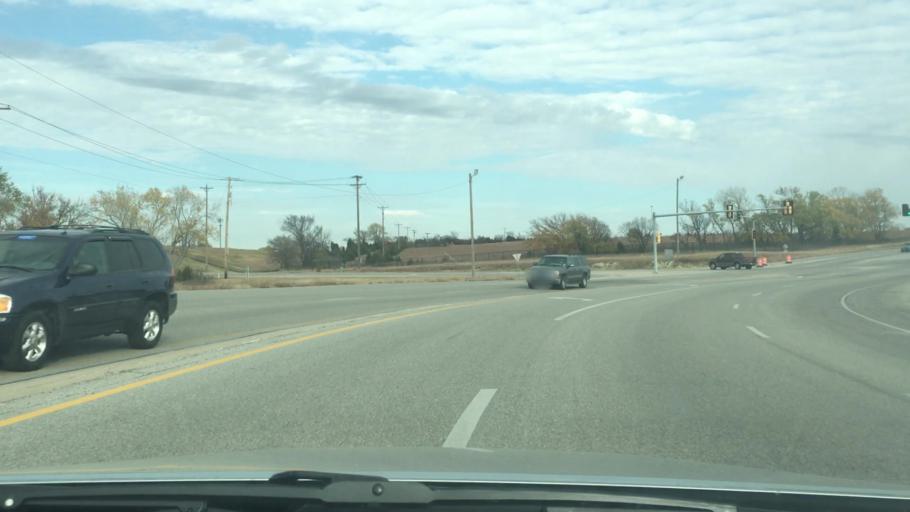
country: US
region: Kansas
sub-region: Sedgwick County
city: Wichita
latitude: 37.6544
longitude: -97.2632
